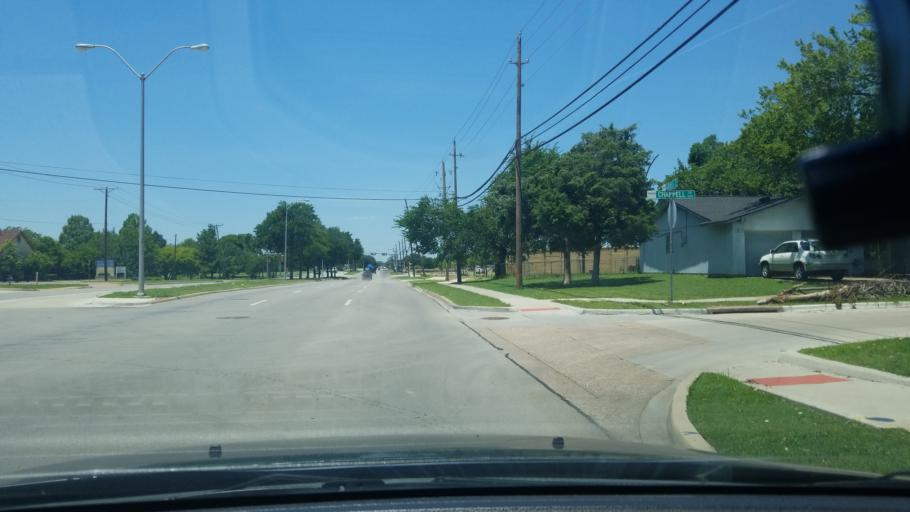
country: US
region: Texas
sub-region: Dallas County
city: Mesquite
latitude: 32.7727
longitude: -96.6142
